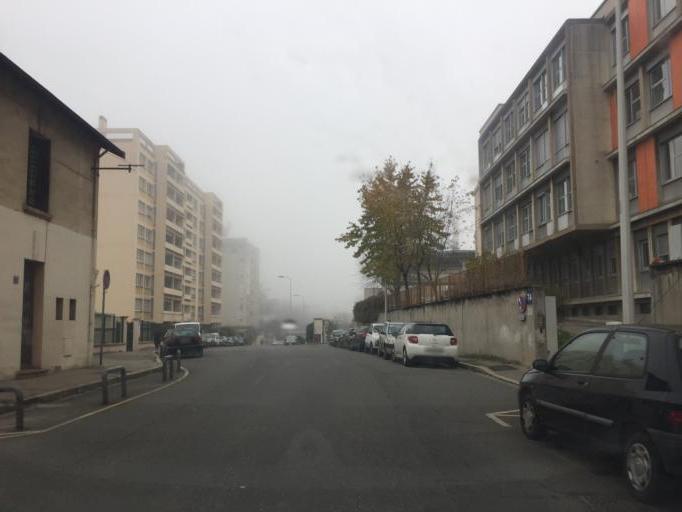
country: FR
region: Rhone-Alpes
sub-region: Departement du Rhone
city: Caluire-et-Cuire
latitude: 45.7806
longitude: 4.8293
